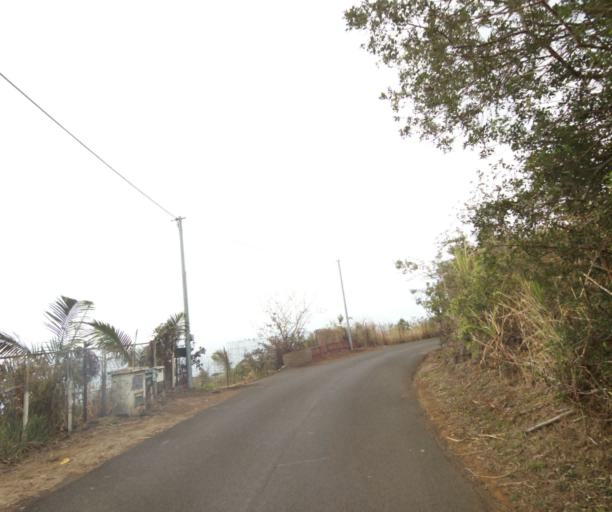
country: RE
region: Reunion
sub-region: Reunion
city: Saint-Paul
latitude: -21.0279
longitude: 55.3010
